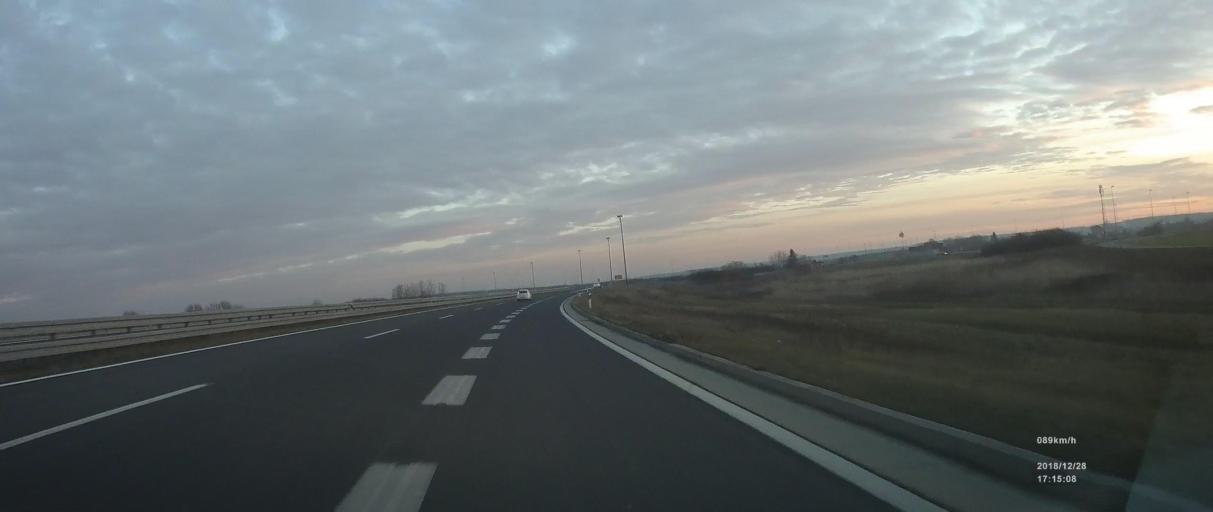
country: HR
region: Zagrebacka
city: Gradici
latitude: 45.6970
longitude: 16.0611
